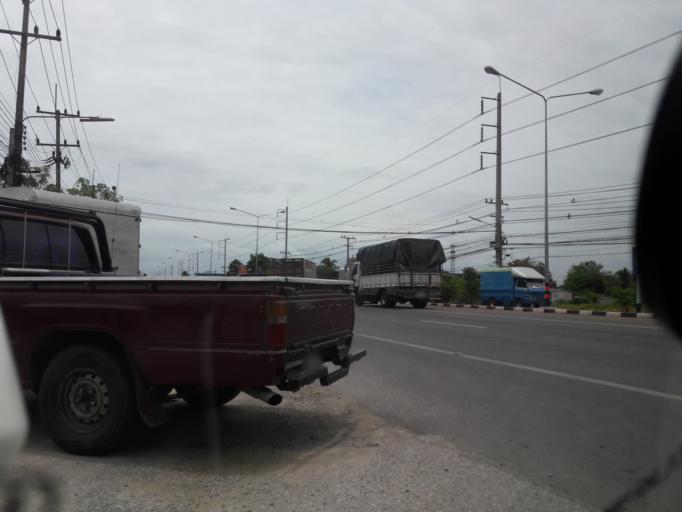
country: TH
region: Ratchaburi
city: Damnoen Saduak
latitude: 13.5674
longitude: 99.9702
